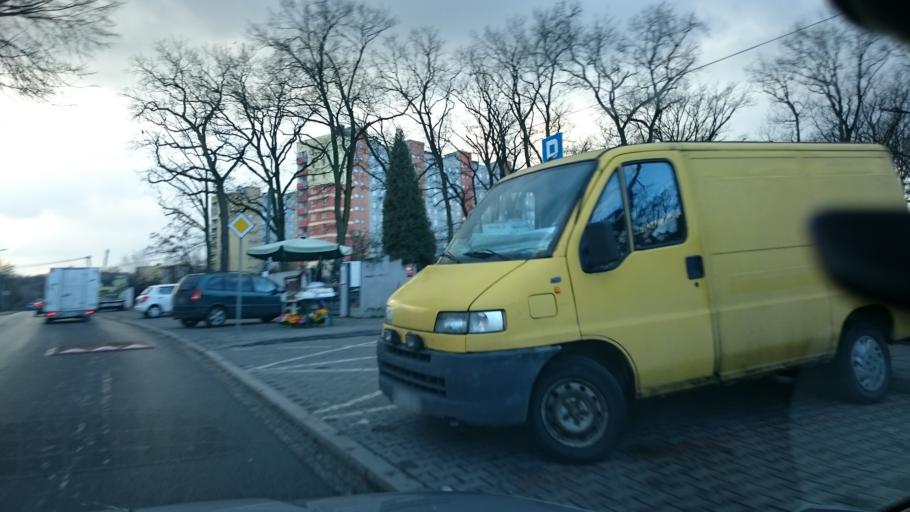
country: PL
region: Lesser Poland Voivodeship
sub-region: Powiat wielicki
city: Czarnochowice
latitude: 50.0107
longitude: 20.0230
